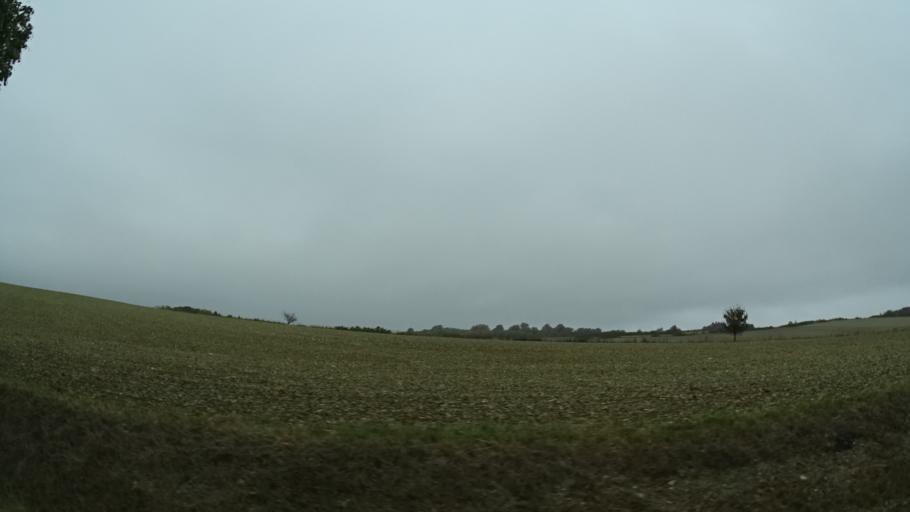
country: DE
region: Thuringia
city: Erbenhausen
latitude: 50.5915
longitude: 10.1484
